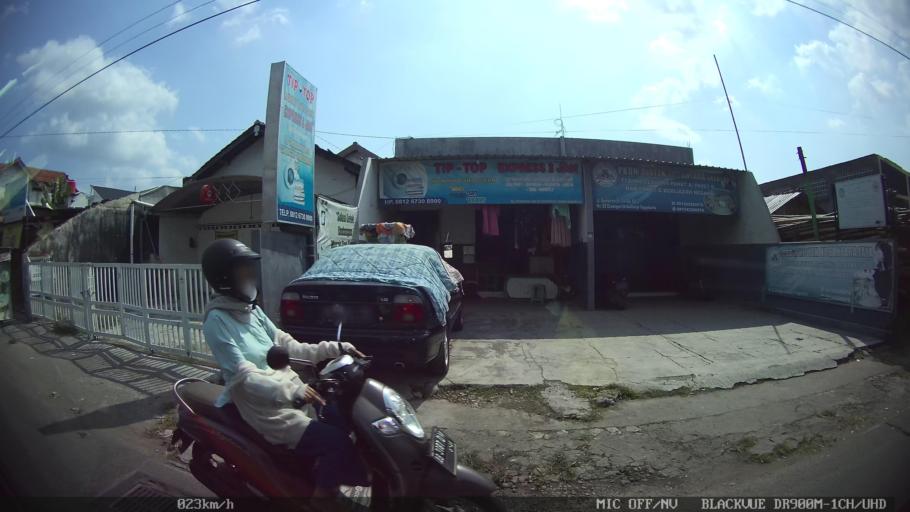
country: ID
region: Daerah Istimewa Yogyakarta
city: Yogyakarta
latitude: -7.8218
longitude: 110.3904
